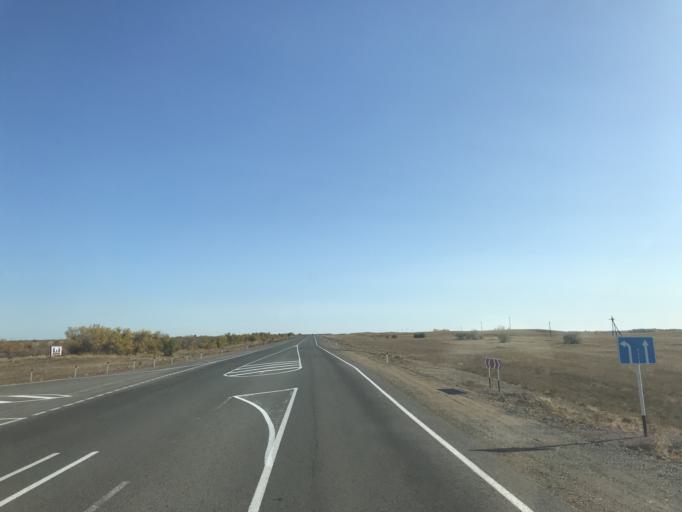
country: KZ
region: Pavlodar
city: Koktobe
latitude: 51.8006
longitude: 77.4816
